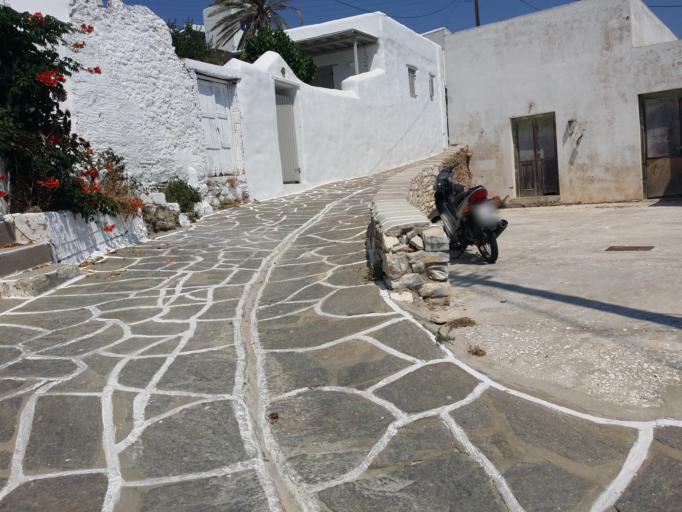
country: GR
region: South Aegean
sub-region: Nomos Kykladon
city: Naousa
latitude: 37.0445
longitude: 25.2496
